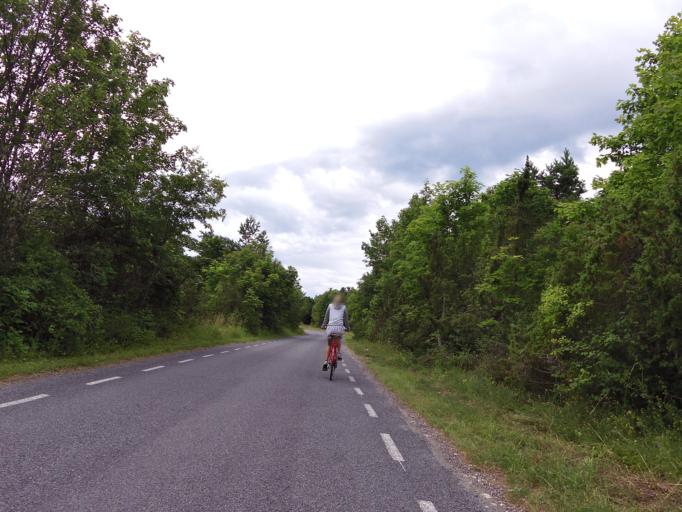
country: EE
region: Hiiumaa
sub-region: Kaerdla linn
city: Kardla
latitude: 58.7861
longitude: 22.8301
